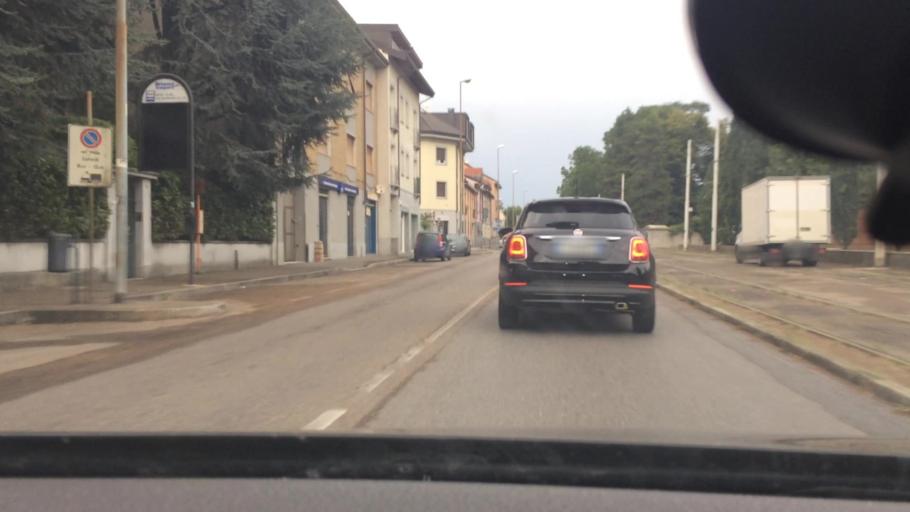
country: IT
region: Lombardy
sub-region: Provincia di Monza e Brianza
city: Nova Milanese
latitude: 45.5898
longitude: 9.1971
